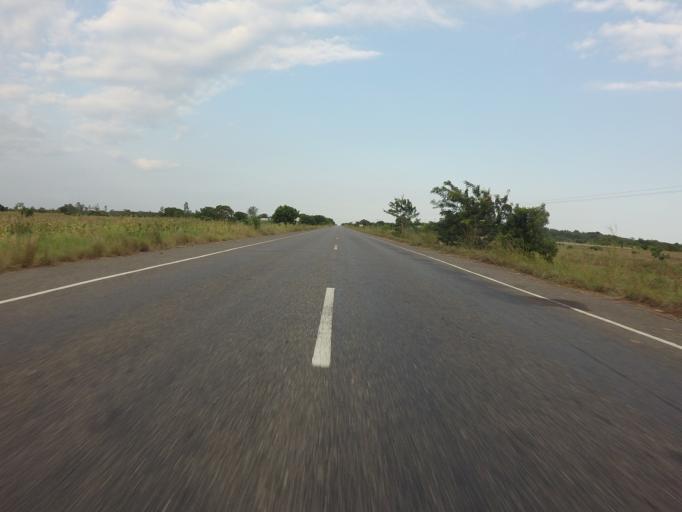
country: GH
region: Volta
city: Anloga
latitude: 6.0884
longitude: 0.5391
